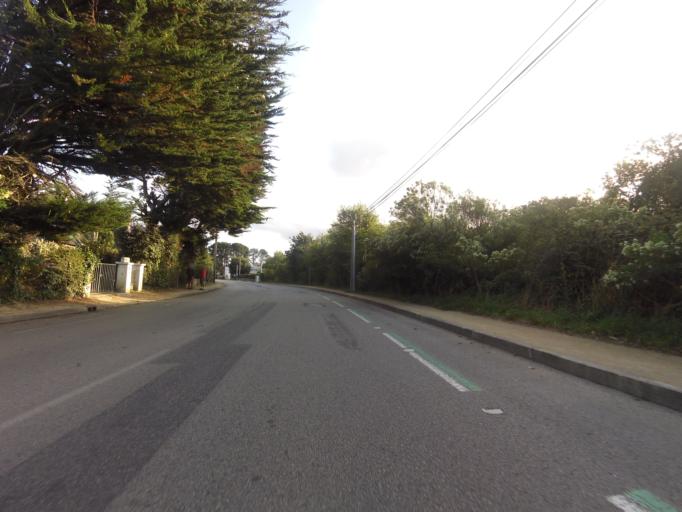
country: FR
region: Brittany
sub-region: Departement du Morbihan
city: Carnac
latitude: 47.5802
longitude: -3.0756
